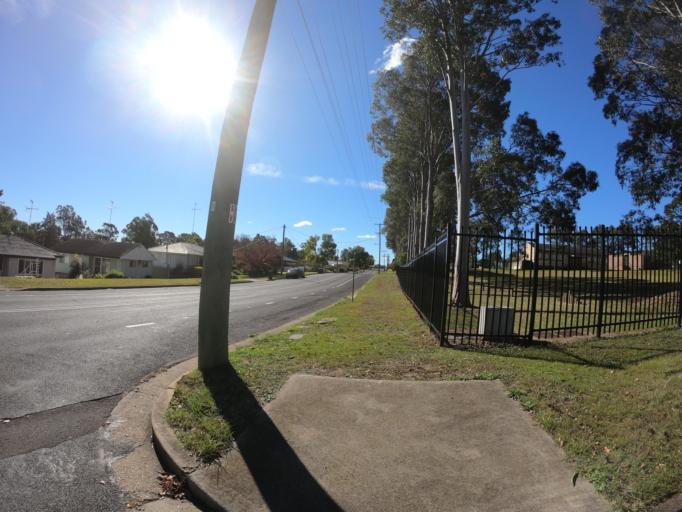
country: AU
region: New South Wales
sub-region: Hawkesbury
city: South Windsor
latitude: -33.6187
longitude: 150.8027
